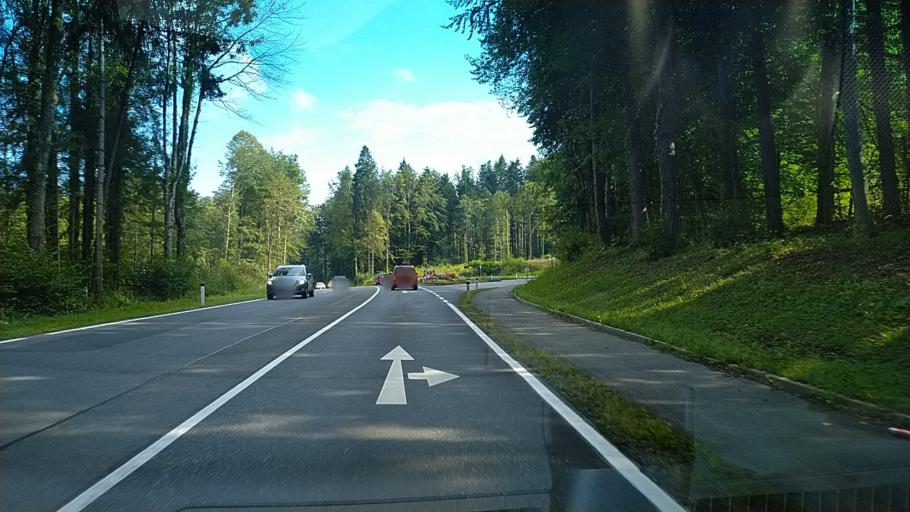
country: AT
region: Styria
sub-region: Politischer Bezirk Deutschlandsberg
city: Hollenegg
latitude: 46.7919
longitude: 15.2231
